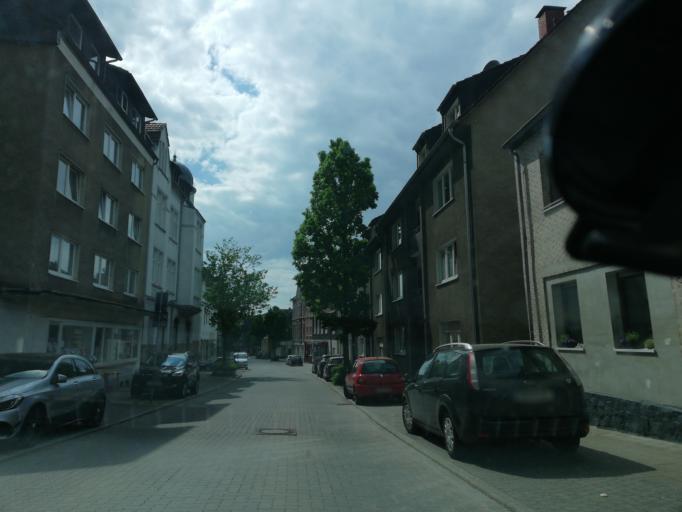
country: DE
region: North Rhine-Westphalia
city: Wetter (Ruhr)
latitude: 51.3877
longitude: 7.3911
